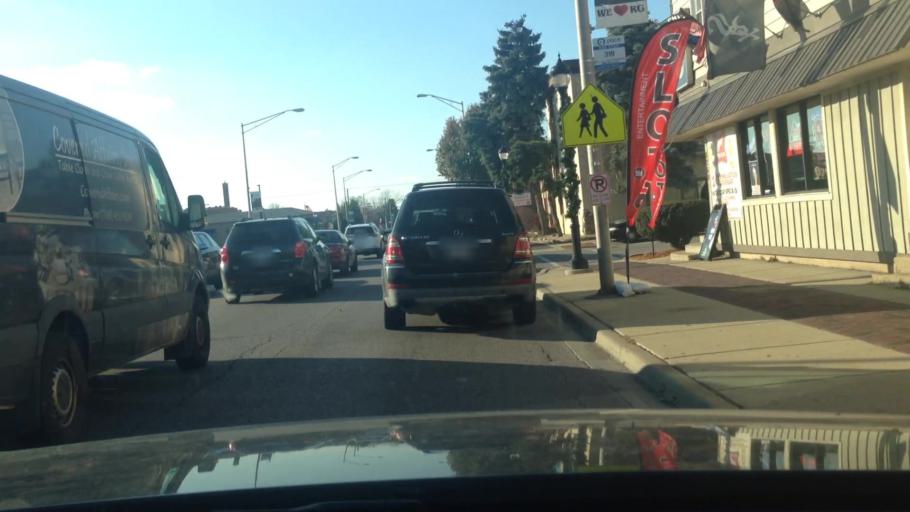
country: US
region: Illinois
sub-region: Cook County
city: River Grove
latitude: 41.9283
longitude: -87.8329
